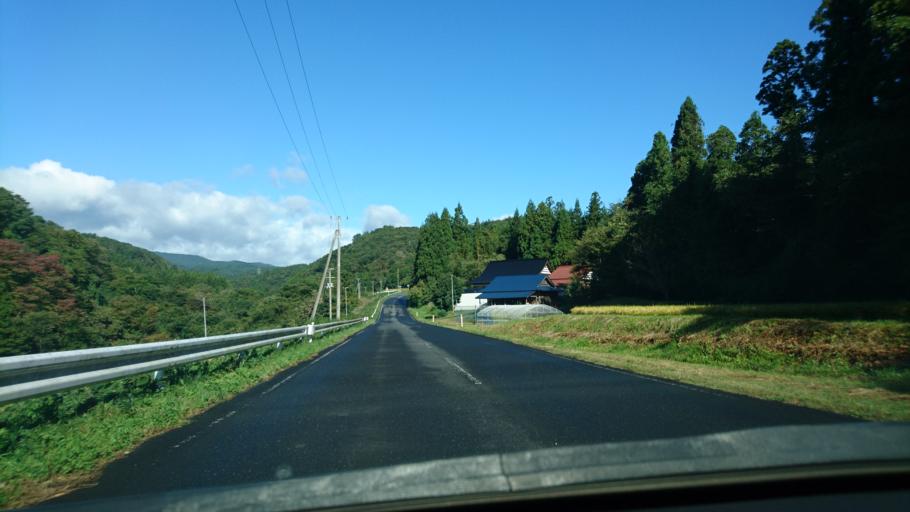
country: JP
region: Iwate
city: Ichinoseki
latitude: 39.0218
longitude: 141.0211
